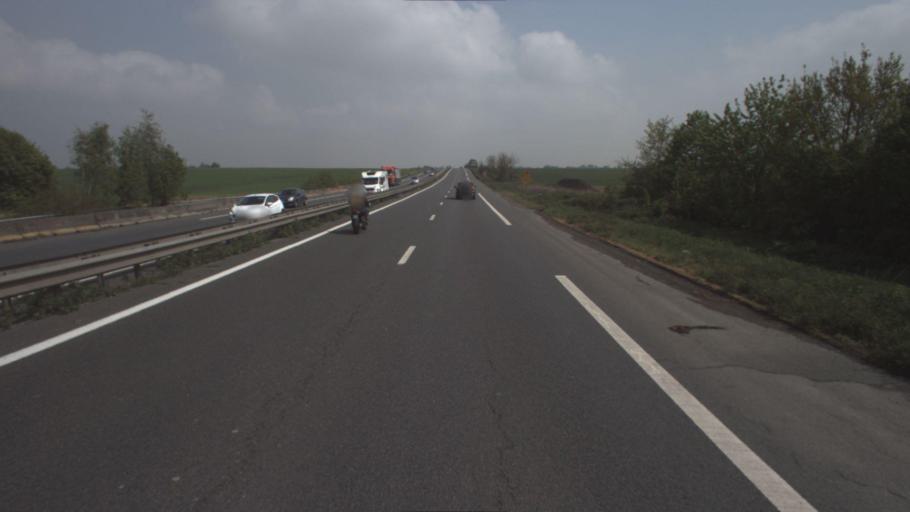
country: FR
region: Picardie
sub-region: Departement de l'Oise
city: Lagny-le-Sec
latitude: 49.0753
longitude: 2.7218
